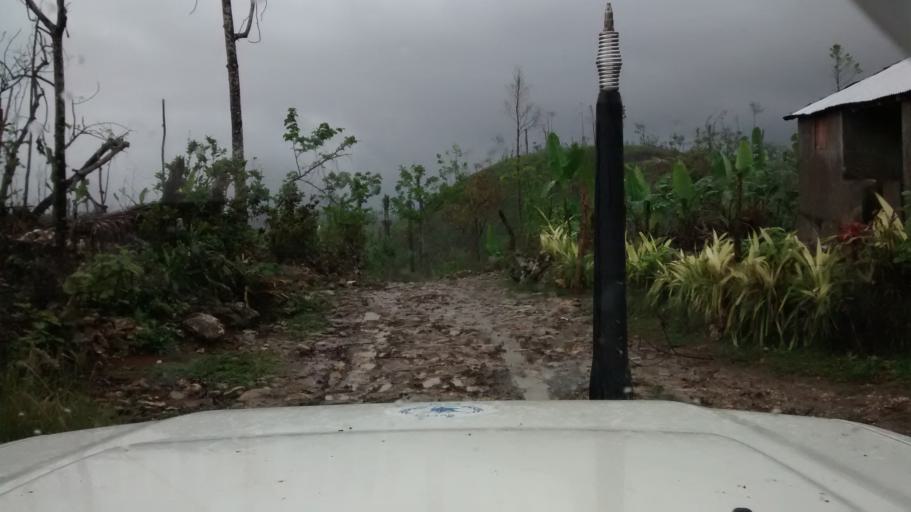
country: HT
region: Grandans
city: Moron
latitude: 18.5290
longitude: -74.1554
